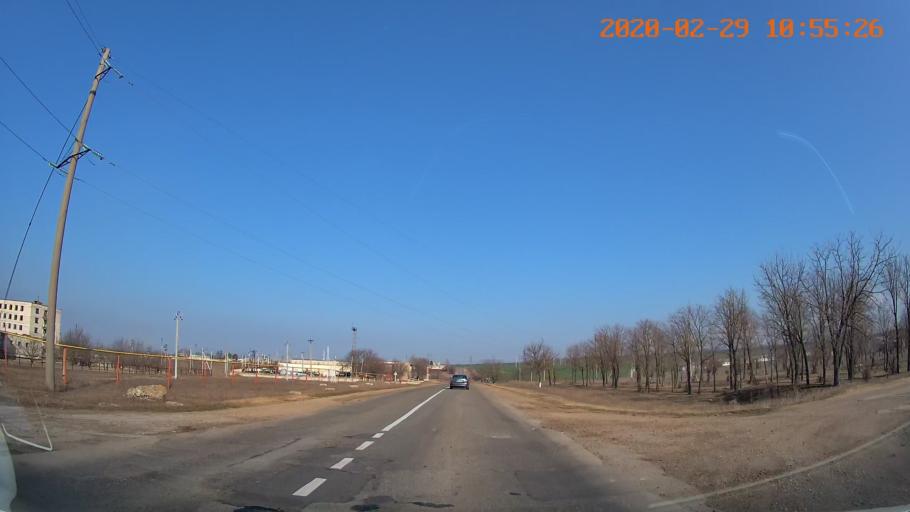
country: MD
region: Telenesti
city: Grigoriopol
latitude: 47.1337
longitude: 29.3251
